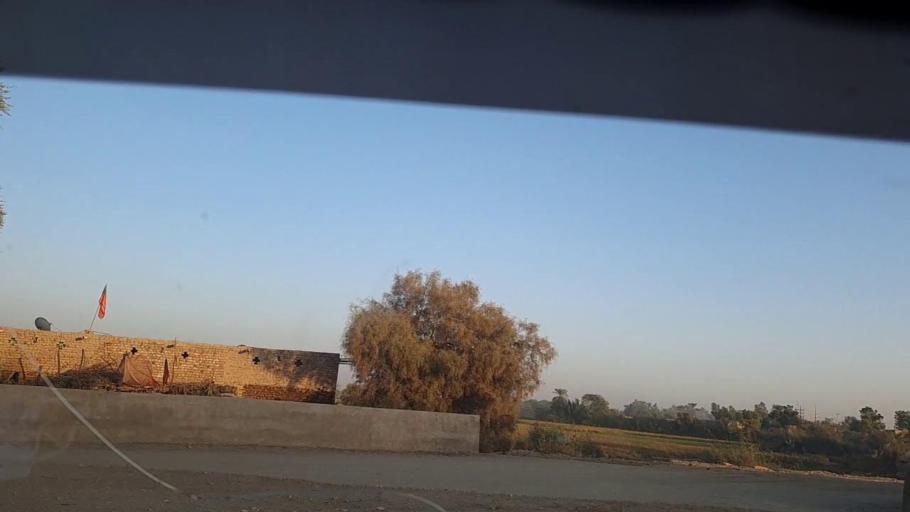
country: PK
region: Sindh
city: Ratodero
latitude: 27.9037
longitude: 68.2403
